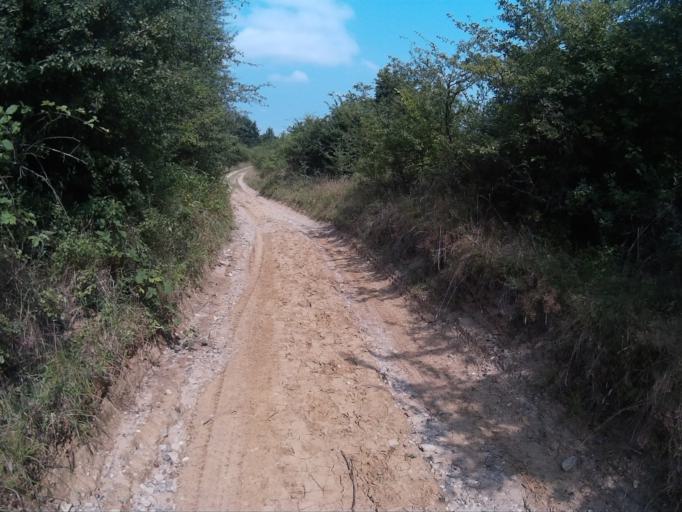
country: HU
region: Veszprem
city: Papa
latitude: 47.2901
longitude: 17.6192
